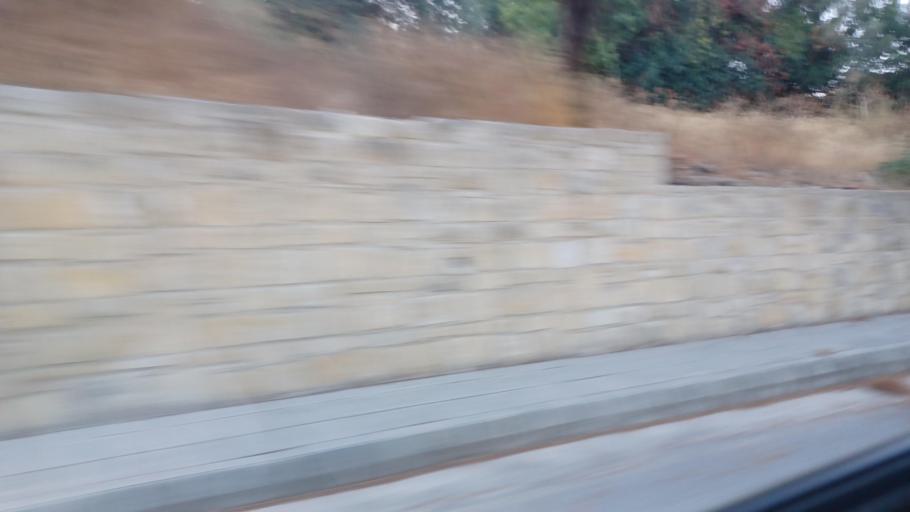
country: CY
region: Pafos
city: Mesogi
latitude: 34.8223
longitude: 32.5835
